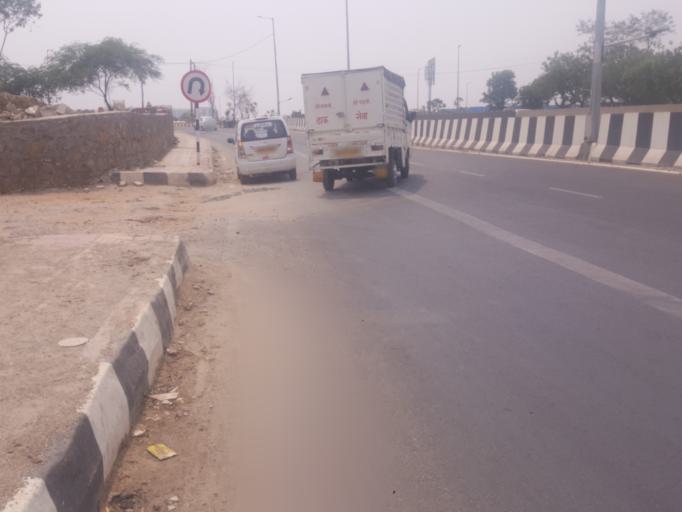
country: IN
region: NCT
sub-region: Central Delhi
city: Karol Bagh
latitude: 28.5527
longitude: 77.1327
